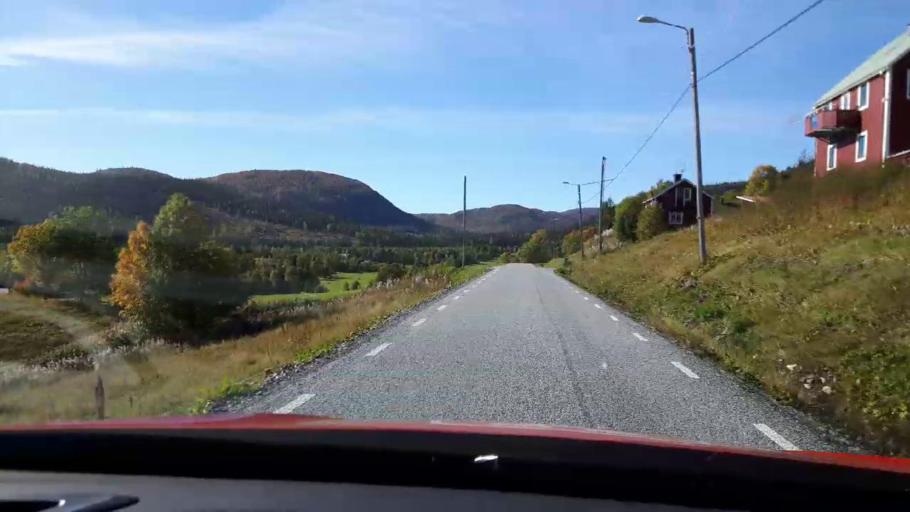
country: NO
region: Nord-Trondelag
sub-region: Royrvik
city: Royrvik
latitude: 64.7285
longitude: 13.9672
